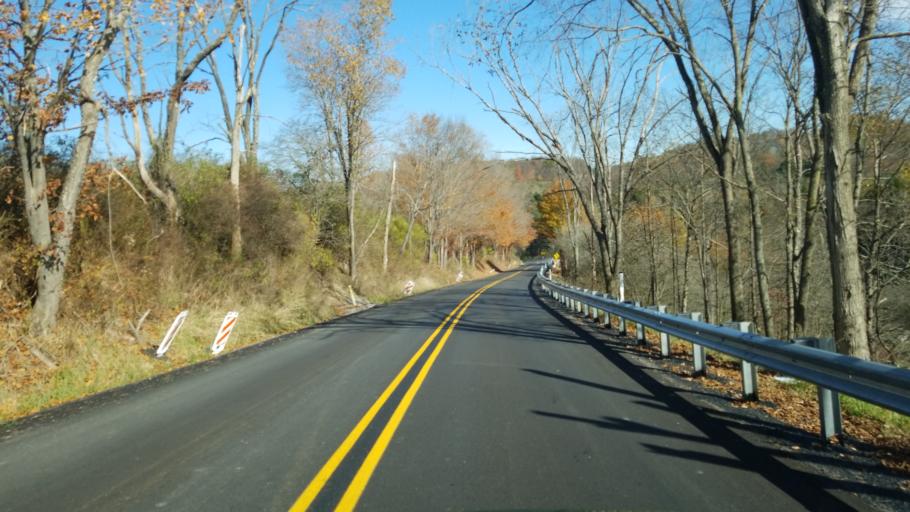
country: US
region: Pennsylvania
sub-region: Jefferson County
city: Brockway
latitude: 41.2331
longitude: -78.8025
